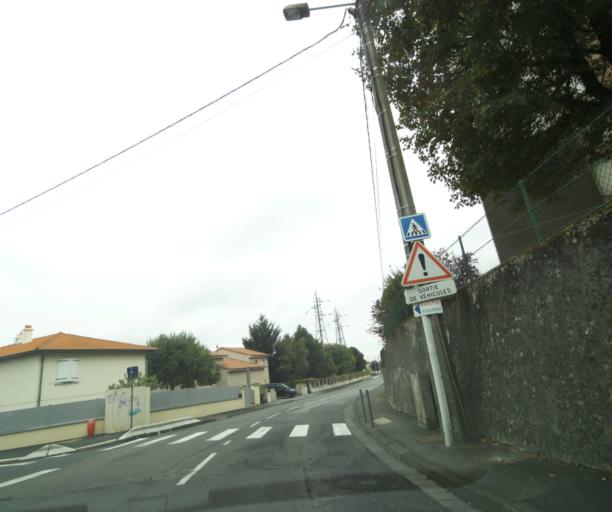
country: FR
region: Auvergne
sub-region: Departement du Puy-de-Dome
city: Durtol
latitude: 45.7893
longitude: 3.0550
